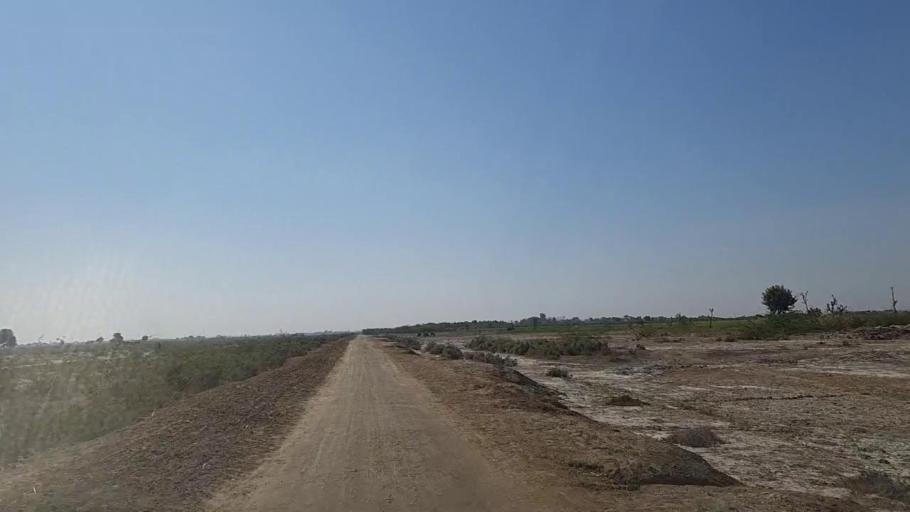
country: PK
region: Sindh
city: Pithoro
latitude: 25.4260
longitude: 69.3769
